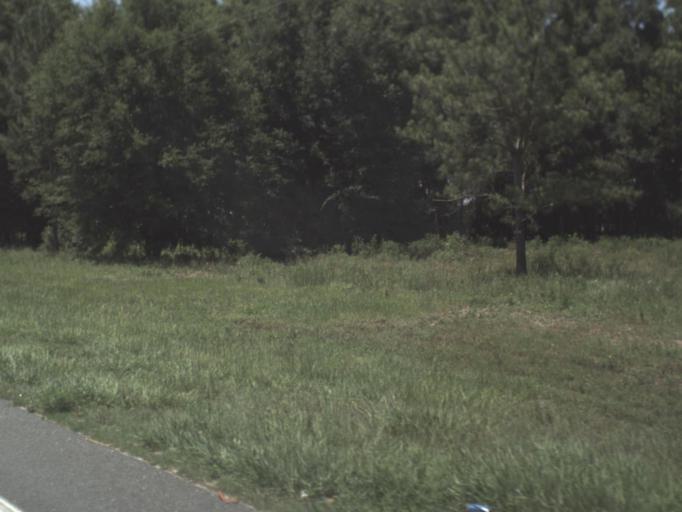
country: US
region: Florida
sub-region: Lafayette County
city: Mayo
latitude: 30.0634
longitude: -83.1925
